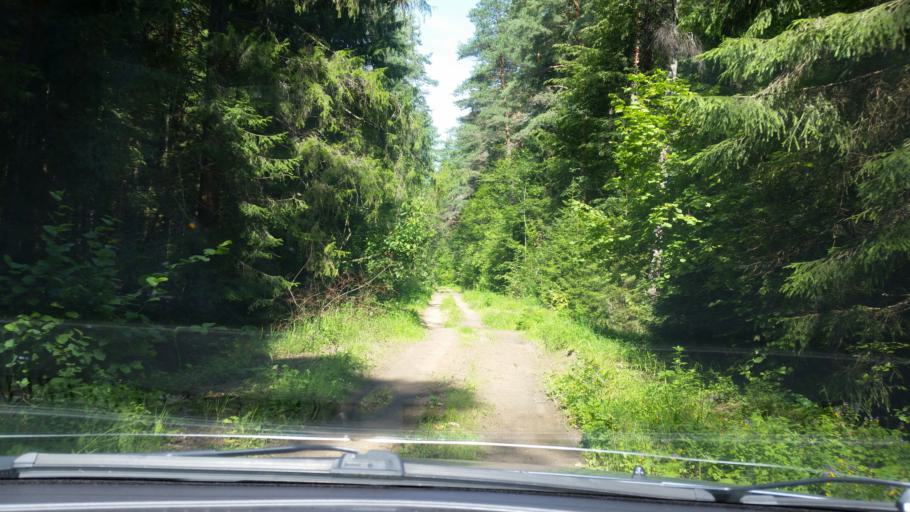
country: RU
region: Moskovskaya
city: Bol'shoye Gryzlovo
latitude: 54.9058
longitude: 37.7626
